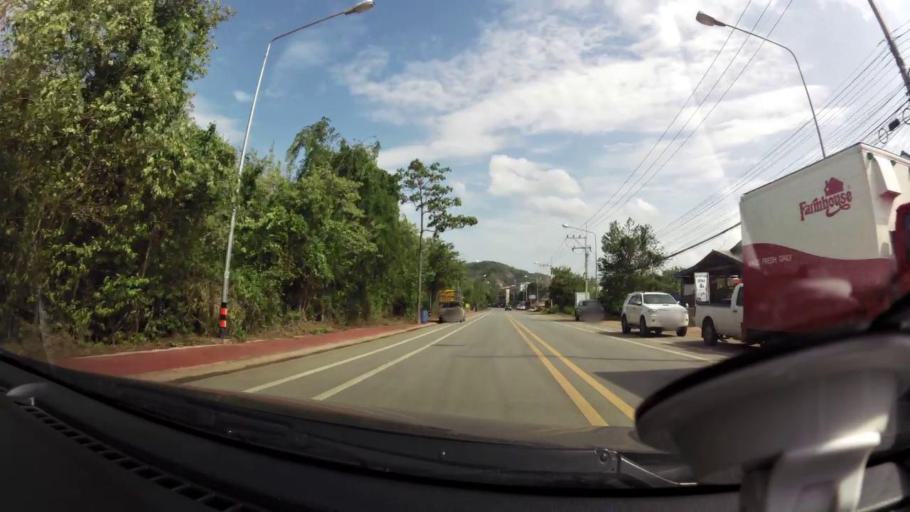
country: TH
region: Prachuap Khiri Khan
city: Hua Hin
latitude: 12.4646
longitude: 99.9742
